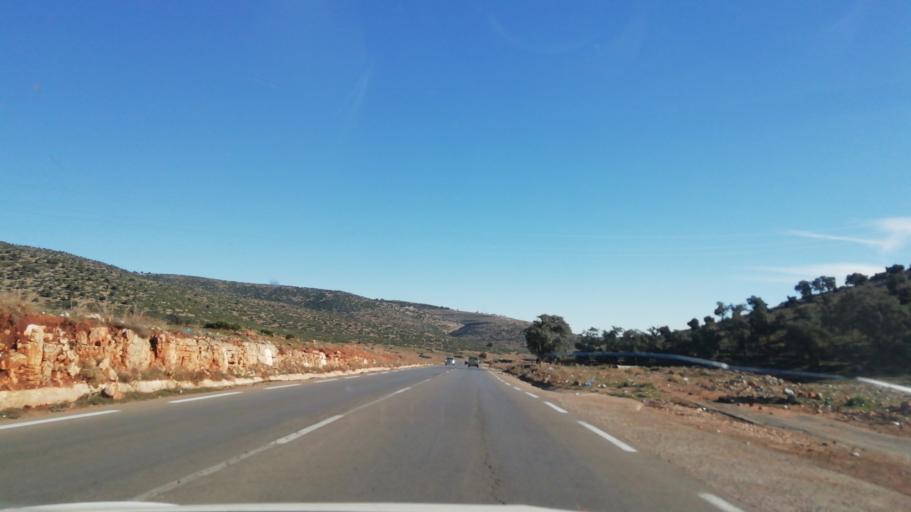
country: DZ
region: Tlemcen
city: Sebdou
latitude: 34.7153
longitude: -1.3290
